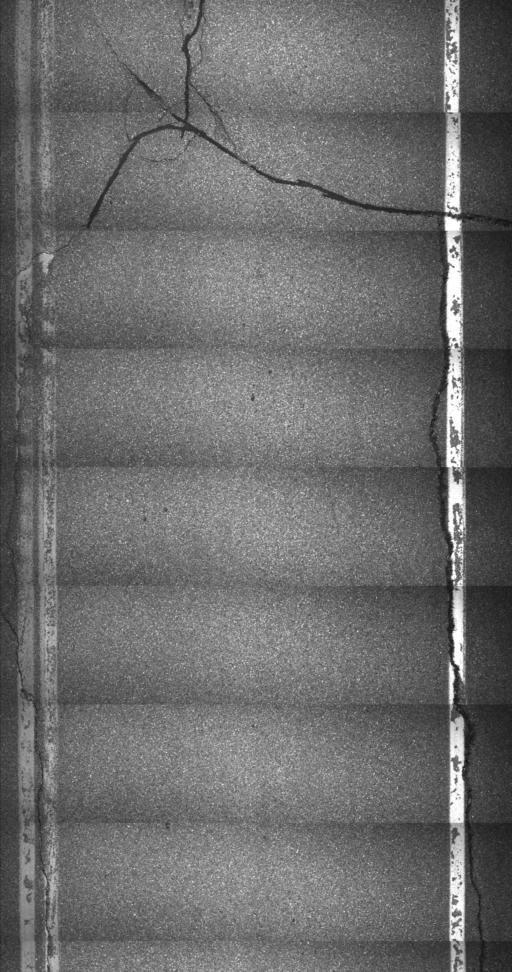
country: US
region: New Hampshire
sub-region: Coos County
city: Colebrook
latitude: 45.0088
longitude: -71.5571
